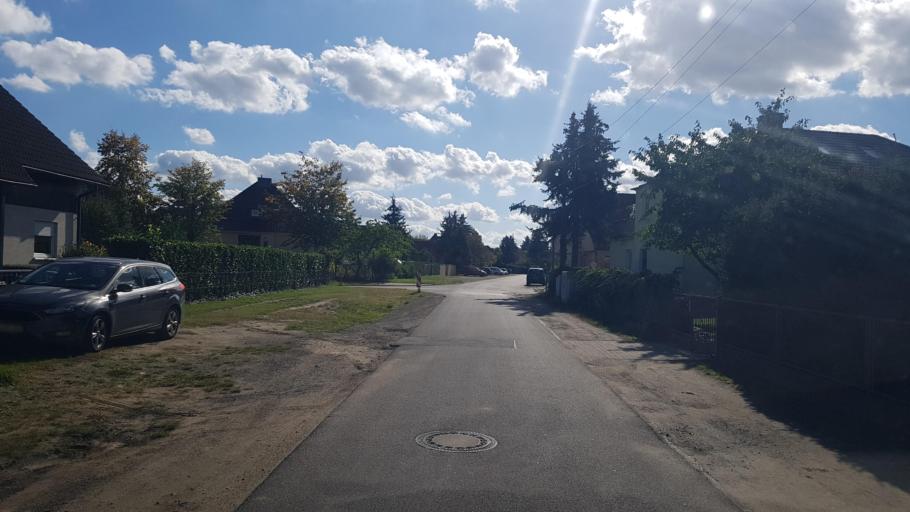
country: DE
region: Brandenburg
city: Cottbus
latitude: 51.7795
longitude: 14.3342
